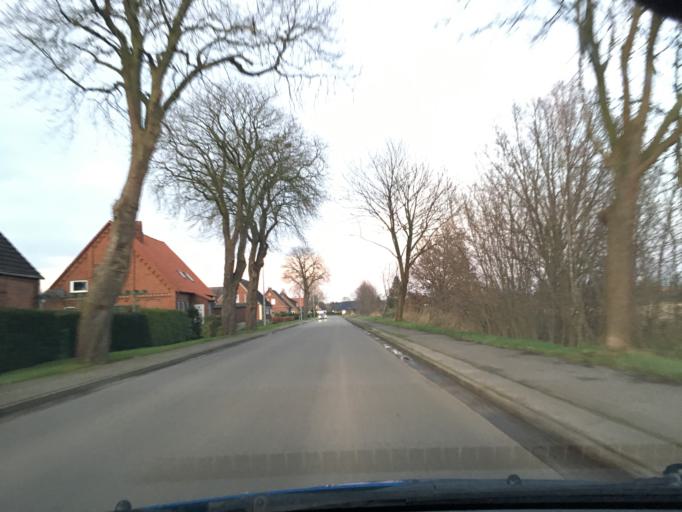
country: DE
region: Lower Saxony
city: Barum
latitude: 53.3652
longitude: 10.4151
